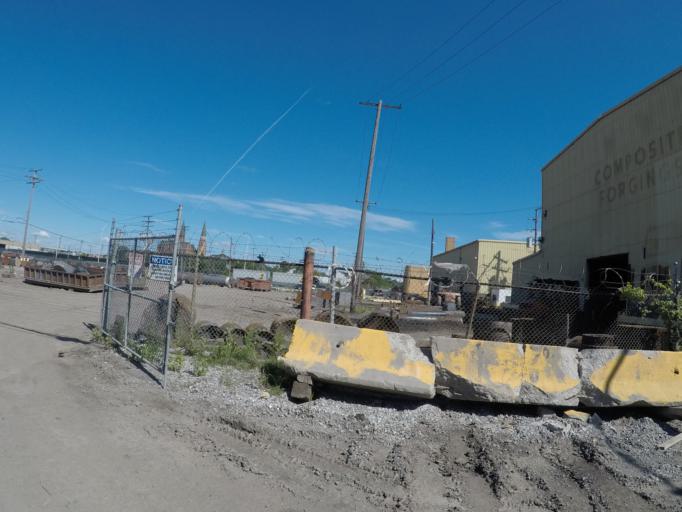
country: US
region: Michigan
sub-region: Wayne County
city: Detroit
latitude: 42.3188
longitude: -83.0730
